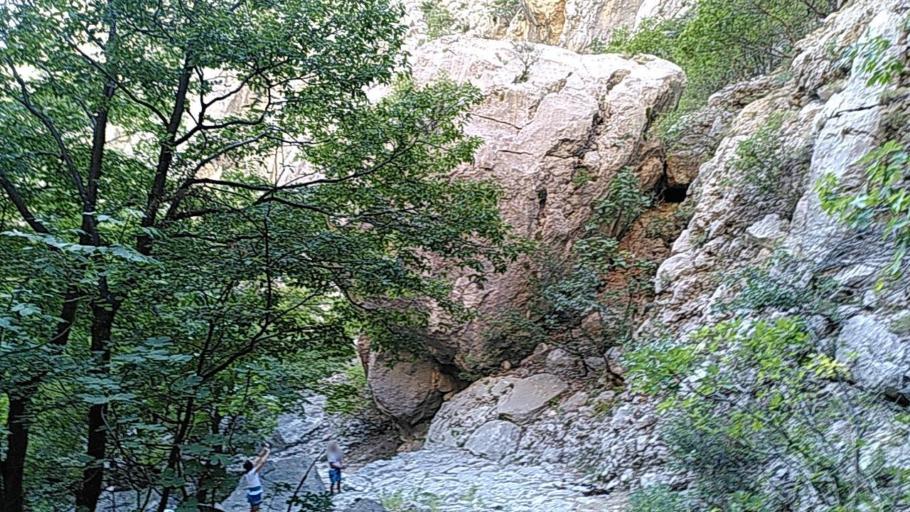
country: HR
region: Zadarska
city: Starigrad
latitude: 44.3078
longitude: 15.4757
